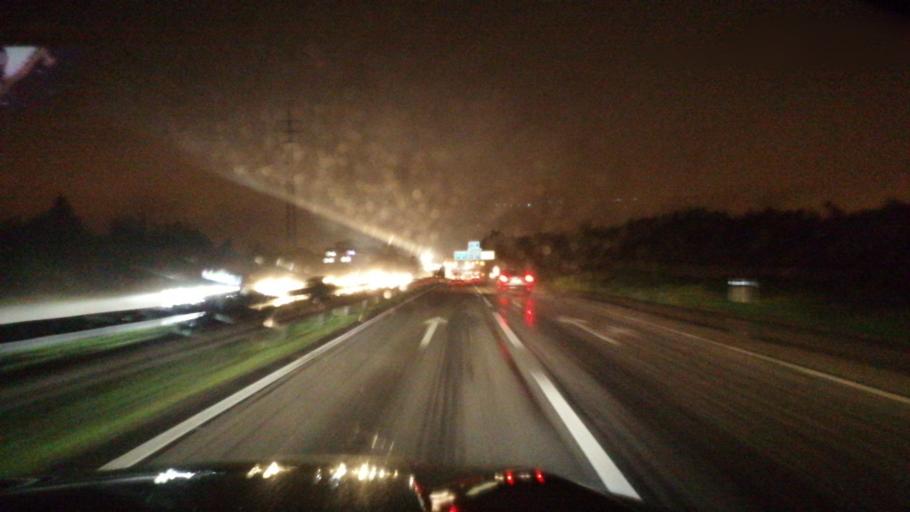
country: PT
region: Porto
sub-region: Vila Nova de Gaia
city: Vila Nova de Gaia
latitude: 41.1138
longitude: -8.6200
